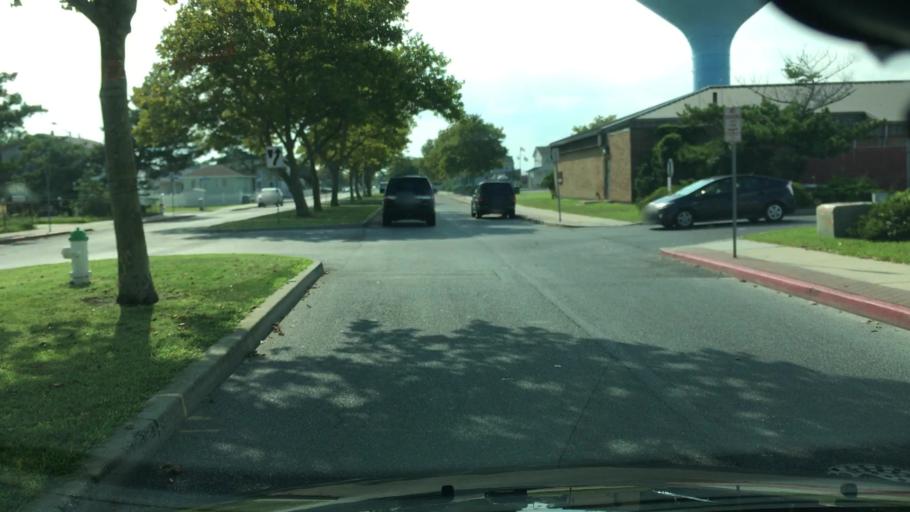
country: US
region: Maryland
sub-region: Worcester County
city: Ocean City
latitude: 38.4095
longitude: -75.0602
